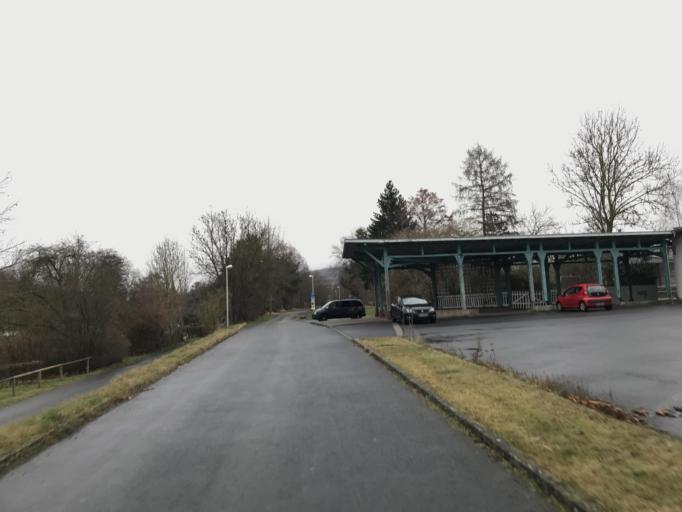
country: DE
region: Hesse
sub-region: Regierungsbezirk Kassel
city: Bad Wildungen
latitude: 51.1200
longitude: 9.1368
